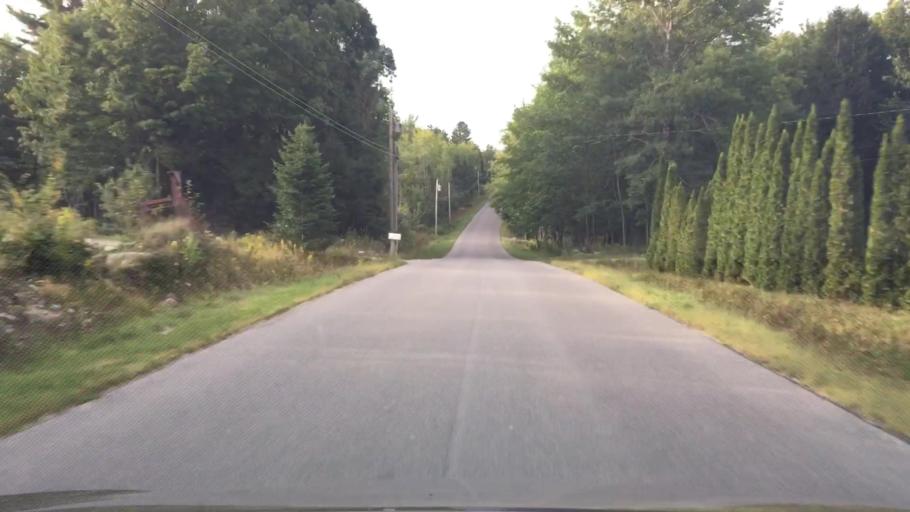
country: US
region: Maine
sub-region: Waldo County
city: Stockton Springs
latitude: 44.4982
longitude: -68.8745
